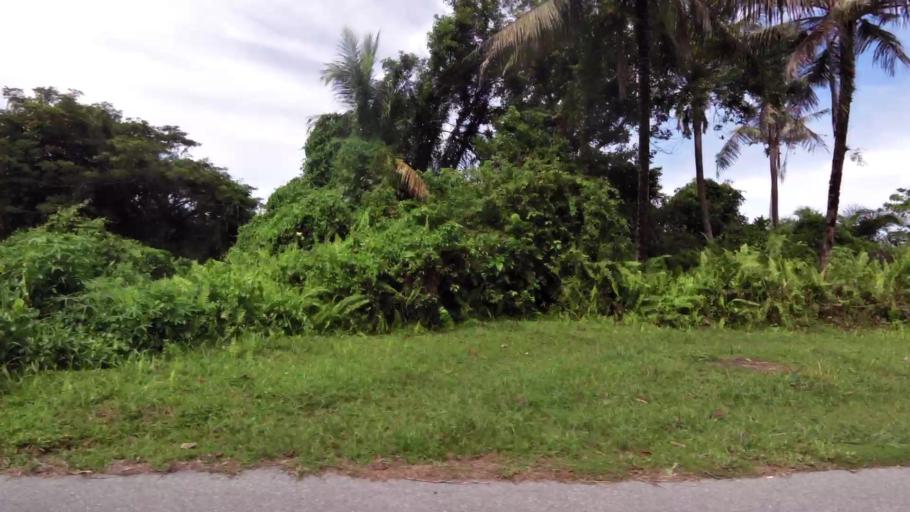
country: BN
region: Belait
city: Seria
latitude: 4.5966
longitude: 114.2835
